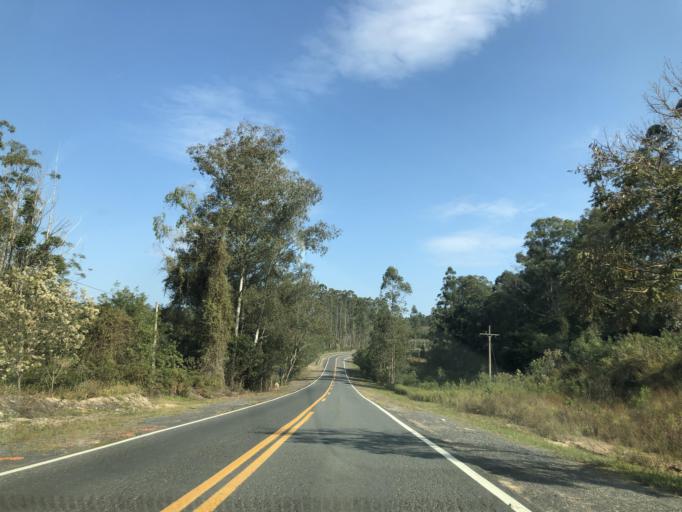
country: BR
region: Sao Paulo
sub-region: Pilar Do Sul
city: Pilar do Sul
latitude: -23.8258
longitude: -47.6645
